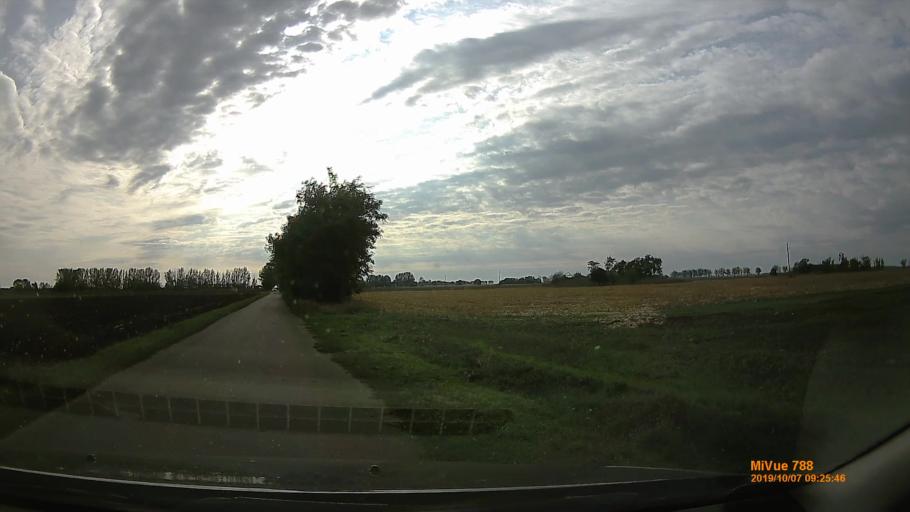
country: HU
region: Bekes
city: Szarvas
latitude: 46.8114
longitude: 20.6559
